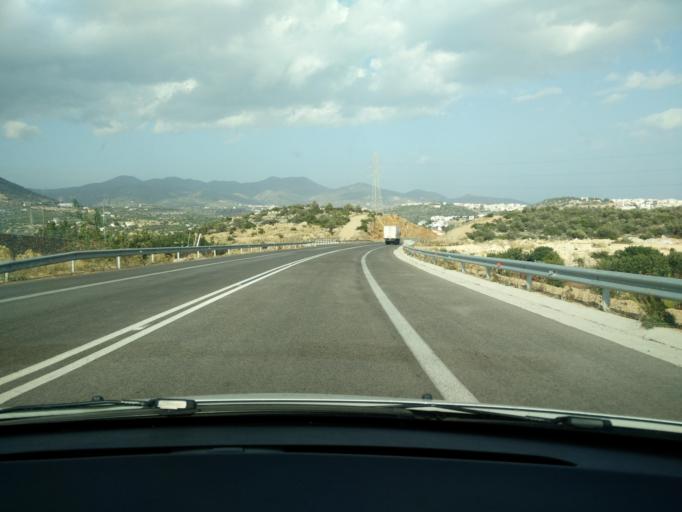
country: GR
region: Crete
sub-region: Nomos Lasithiou
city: Agios Nikolaos
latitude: 35.1776
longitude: 25.7010
